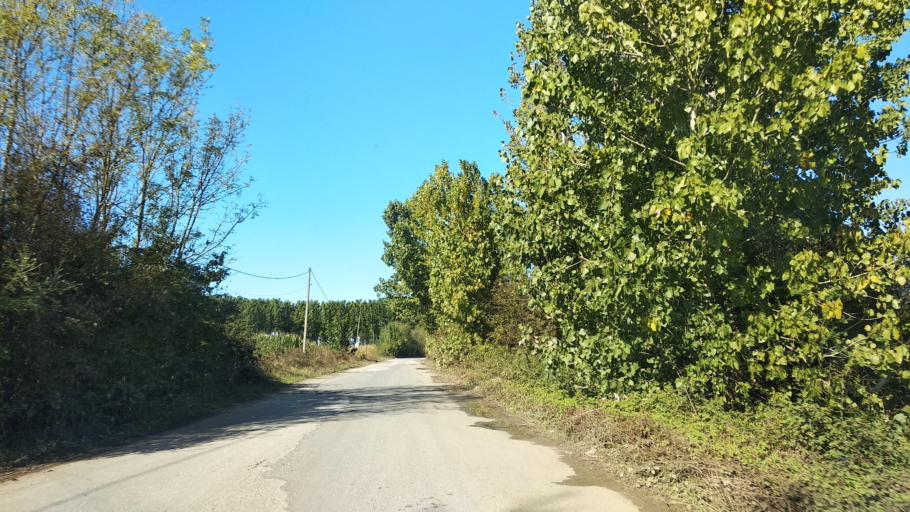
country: TR
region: Sakarya
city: Ortakoy
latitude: 41.0284
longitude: 30.6068
